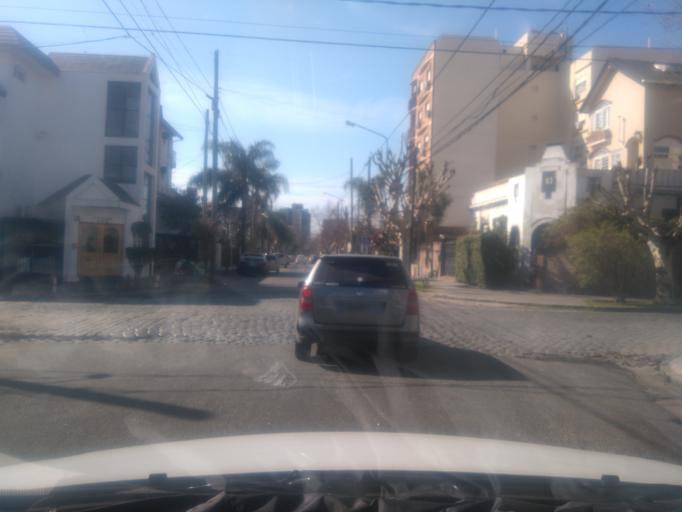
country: AR
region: Buenos Aires
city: San Justo
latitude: -34.6424
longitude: -58.5576
